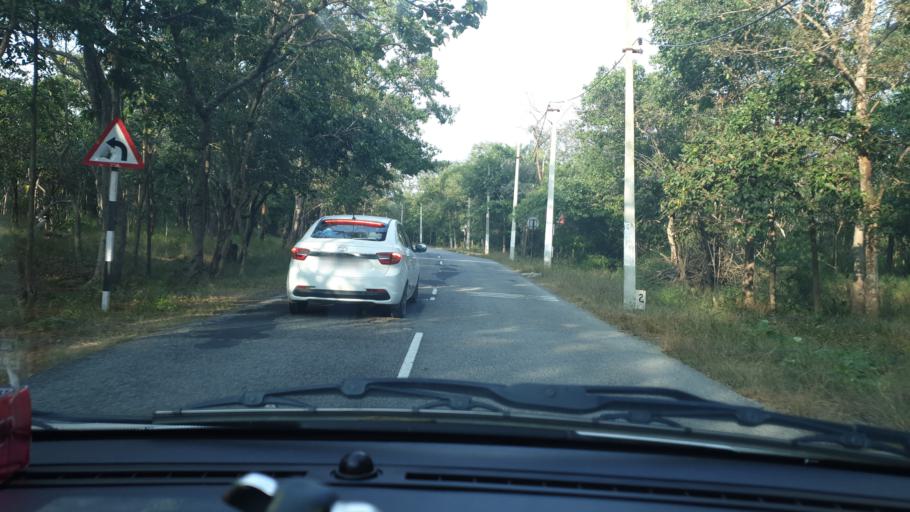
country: IN
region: Andhra Pradesh
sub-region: Kurnool
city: Srisailam
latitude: 16.3043
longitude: 78.7320
